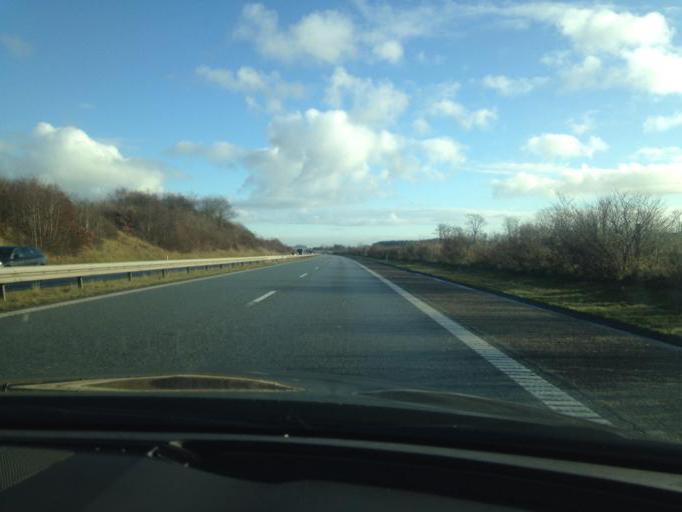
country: DK
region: South Denmark
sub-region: Vejen Kommune
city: Holsted
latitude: 55.5120
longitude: 8.9613
